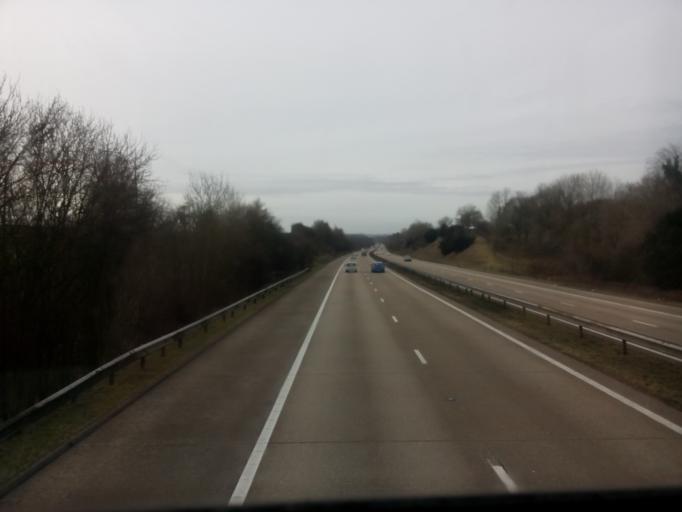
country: GB
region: England
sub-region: Hampshire
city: Overton
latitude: 51.1871
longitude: -1.2103
